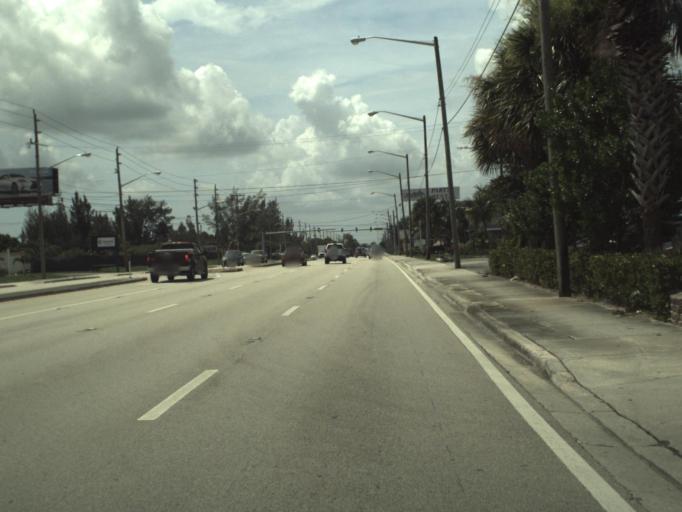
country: US
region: Florida
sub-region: Palm Beach County
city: Lake Clarke Shores
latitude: 26.6606
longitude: -80.0884
